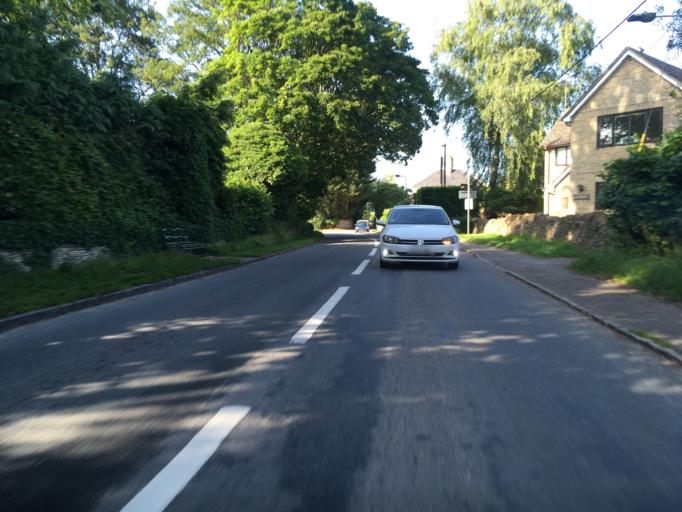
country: GB
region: England
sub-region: Oxfordshire
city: Charlbury
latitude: 51.8760
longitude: -1.4784
